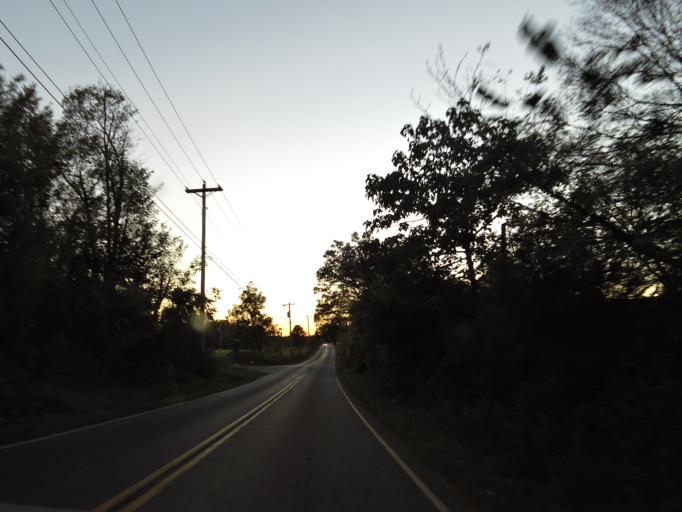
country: US
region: Tennessee
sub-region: Blount County
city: Wildwood
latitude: 35.7758
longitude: -83.8396
